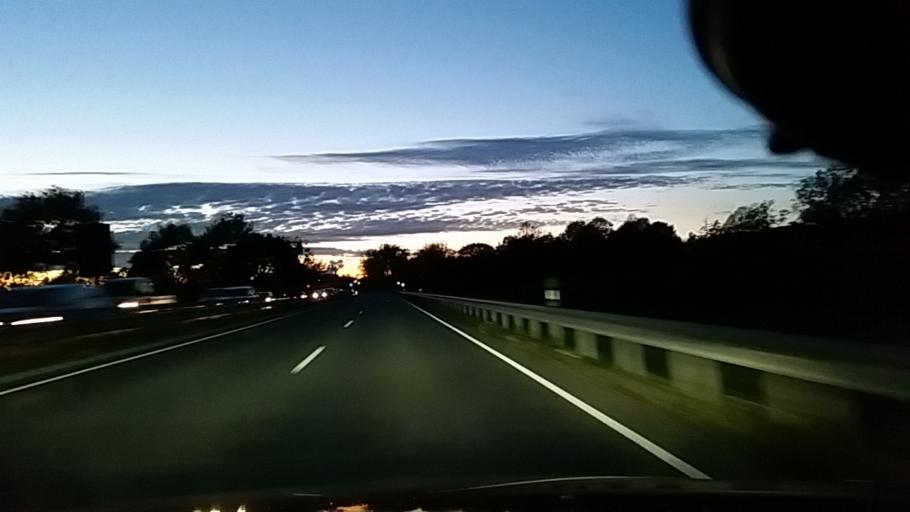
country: DE
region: Lower Saxony
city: Wolfsburg
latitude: 52.4401
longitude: 10.8197
